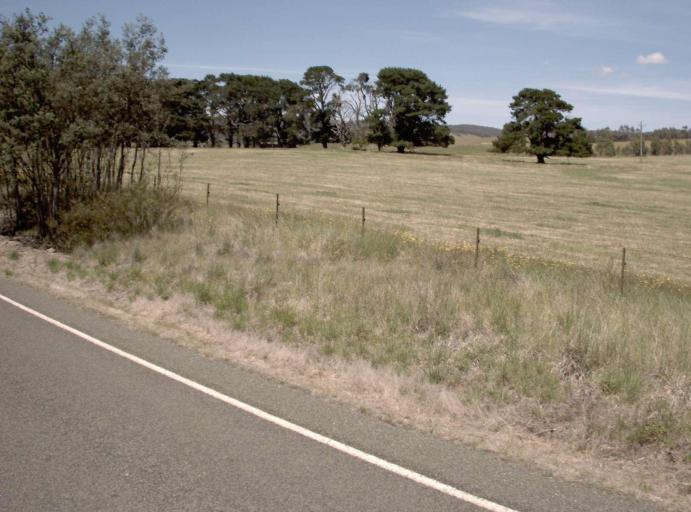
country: AU
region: Victoria
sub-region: Alpine
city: Mount Beauty
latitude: -37.1471
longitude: 147.6482
